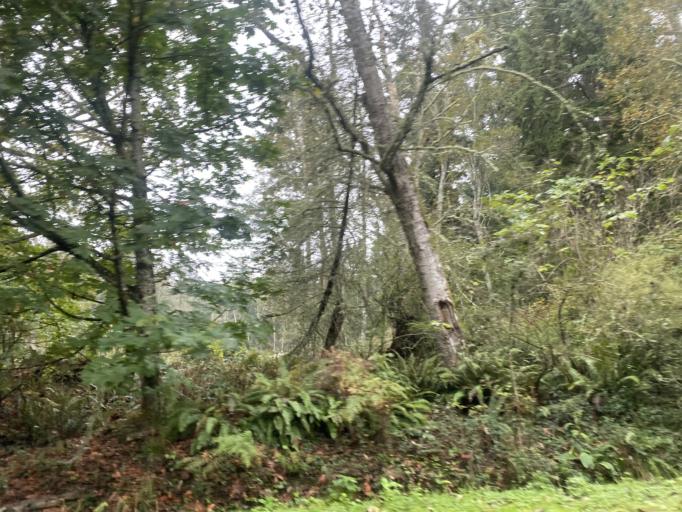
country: US
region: Washington
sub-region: Island County
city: Freeland
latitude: 48.0798
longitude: -122.5613
